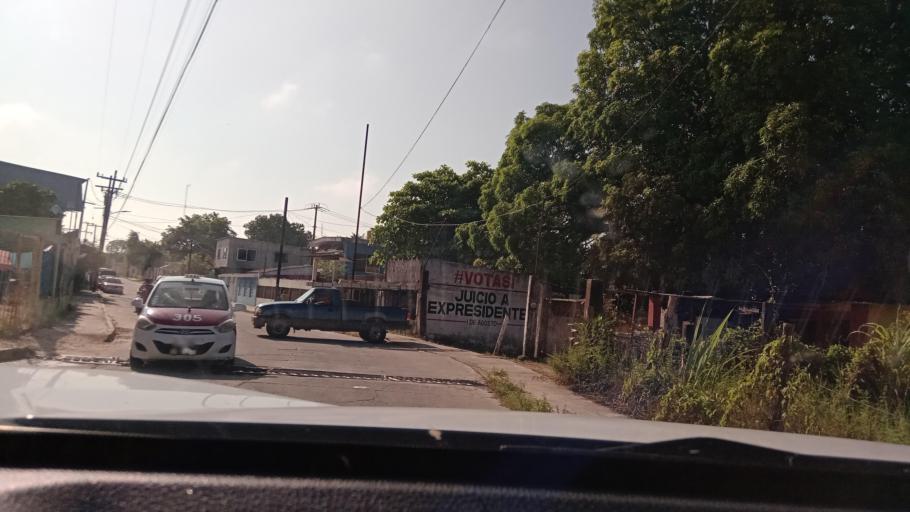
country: MX
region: Veracruz
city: Las Choapas
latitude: 17.9000
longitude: -94.0957
